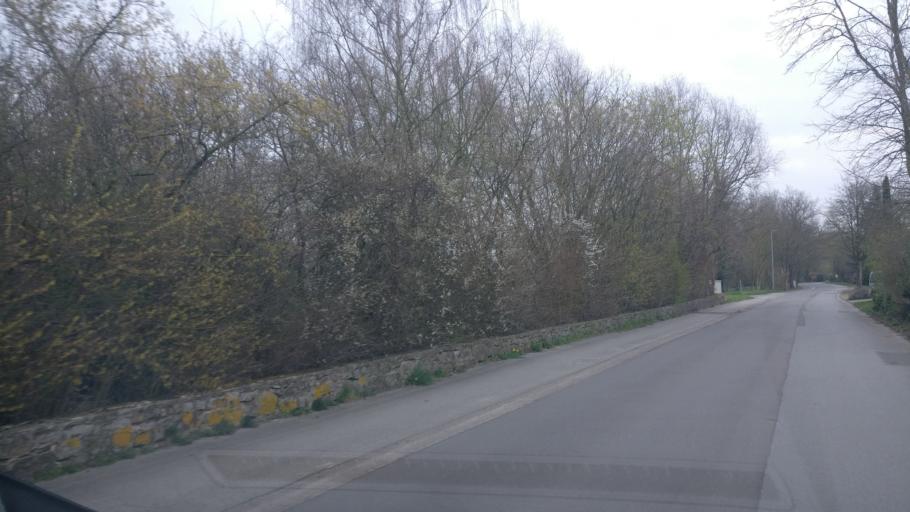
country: DE
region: North Rhine-Westphalia
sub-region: Regierungsbezirk Detmold
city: Lage
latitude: 52.0195
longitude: 8.7697
